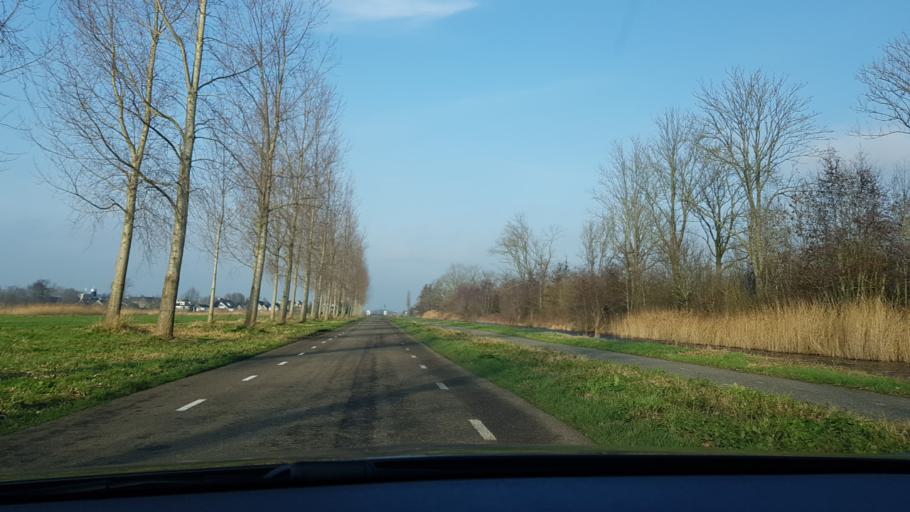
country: NL
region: Utrecht
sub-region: Gemeente De Ronde Venen
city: Mijdrecht
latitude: 52.1919
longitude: 4.9173
